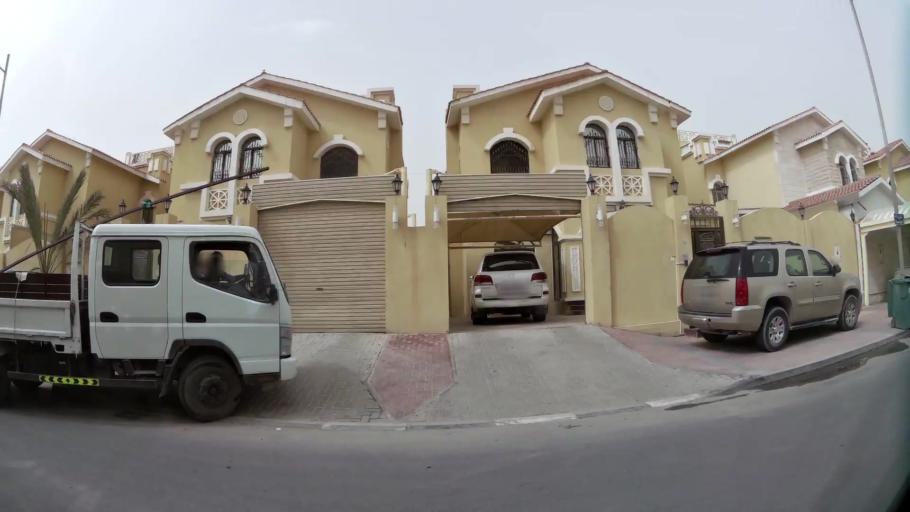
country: QA
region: Baladiyat ad Dawhah
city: Doha
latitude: 25.2294
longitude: 51.5376
